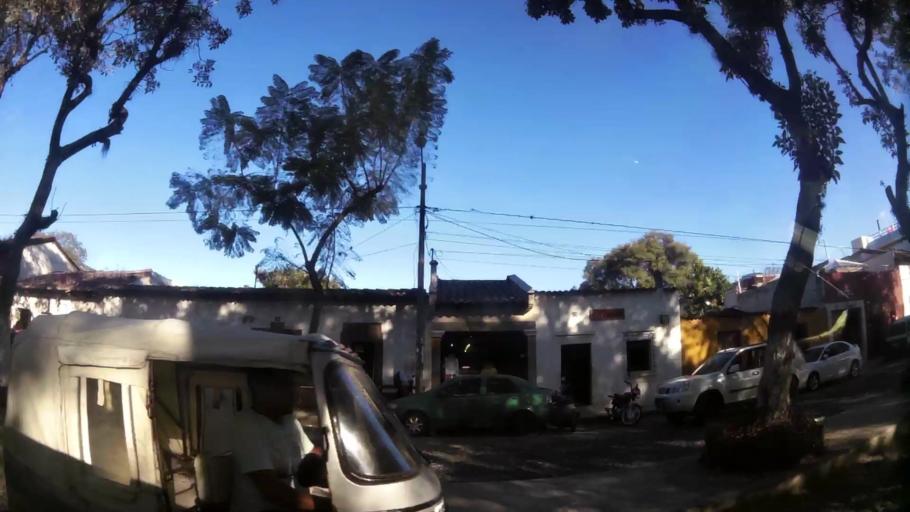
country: GT
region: Sacatepequez
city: Antigua Guatemala
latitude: 14.5604
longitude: -90.7376
